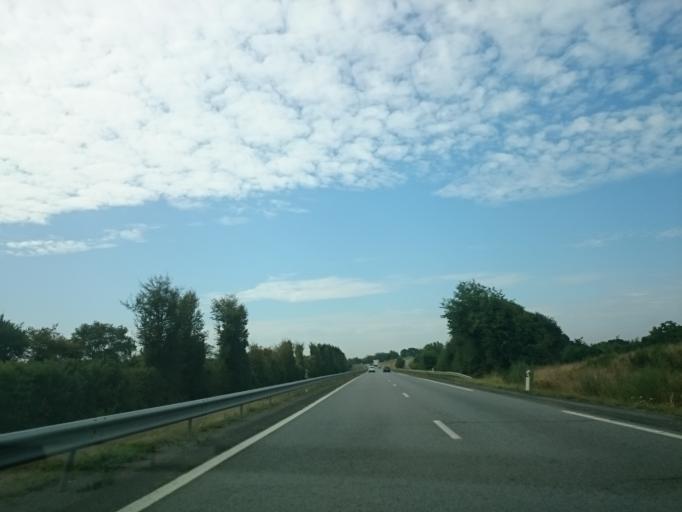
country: FR
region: Brittany
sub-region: Departement d'Ille-et-Vilaine
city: Crevin
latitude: 47.9186
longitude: -1.6801
